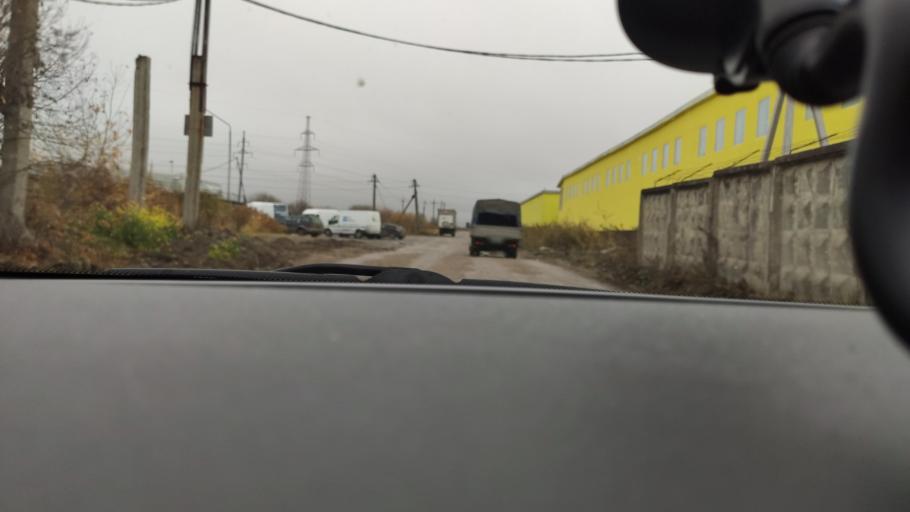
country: RU
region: Perm
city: Gamovo
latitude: 57.9119
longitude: 56.1801
